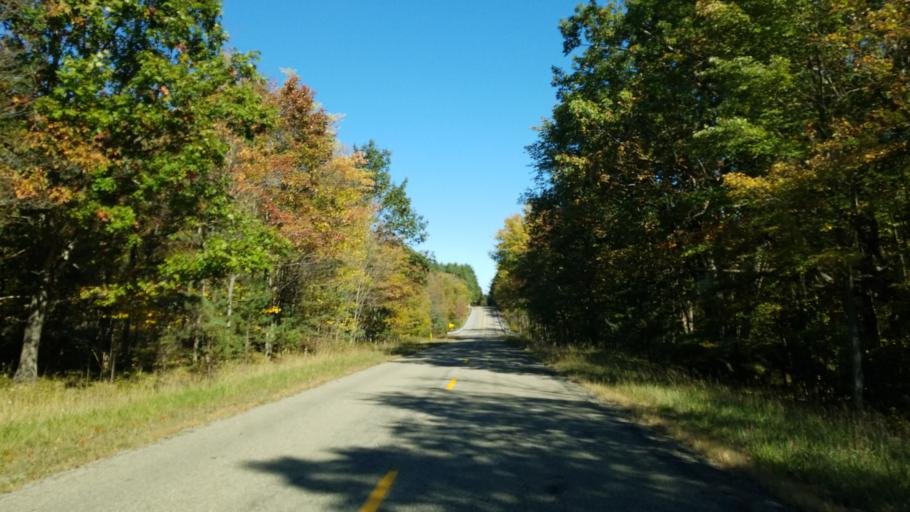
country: US
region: Pennsylvania
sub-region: Clearfield County
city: Shiloh
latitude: 41.2595
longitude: -78.3085
